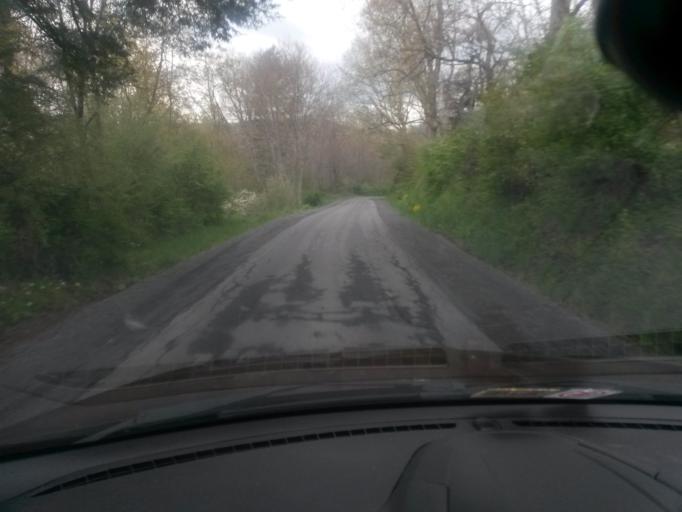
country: US
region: West Virginia
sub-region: Greenbrier County
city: Lewisburg
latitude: 37.9383
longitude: -80.4194
